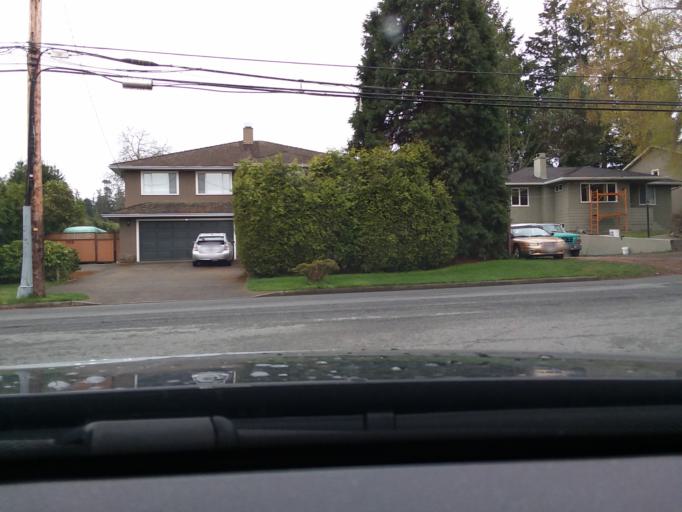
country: CA
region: British Columbia
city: Victoria
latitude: 48.5144
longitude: -123.3786
